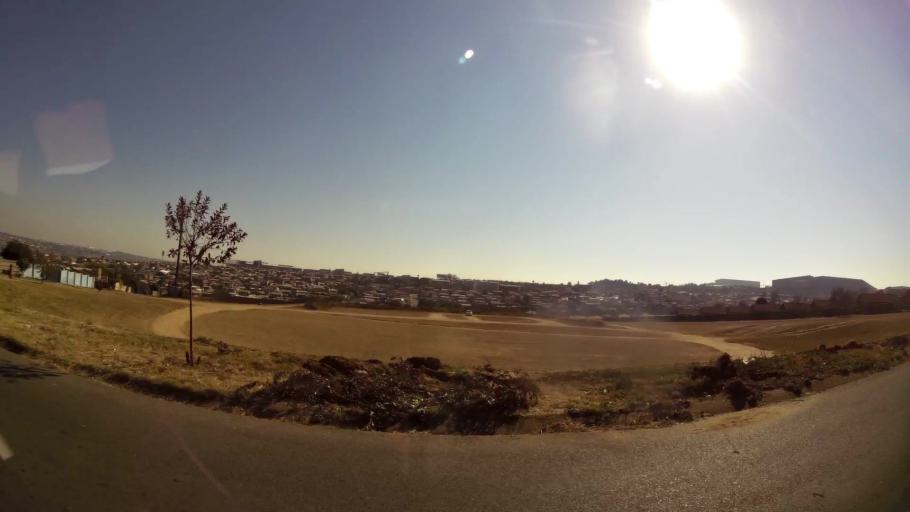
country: ZA
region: Gauteng
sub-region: City of Johannesburg Metropolitan Municipality
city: Modderfontein
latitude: -26.1126
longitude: 28.1225
